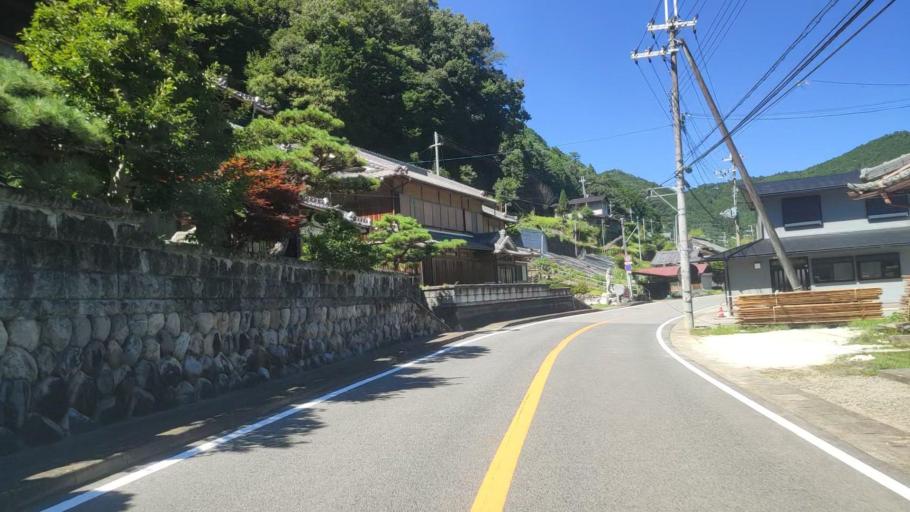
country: JP
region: Nara
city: Yoshino-cho
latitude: 34.3863
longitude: 135.9166
